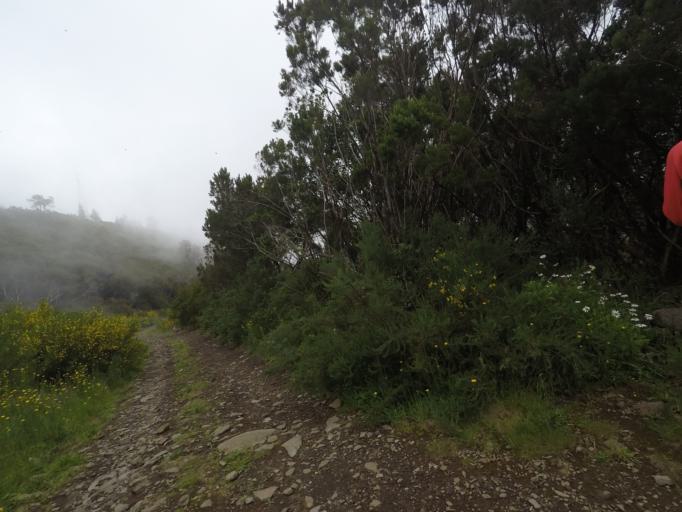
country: PT
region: Madeira
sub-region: Sao Vicente
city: Sao Vicente
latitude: 32.7715
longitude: -17.0649
